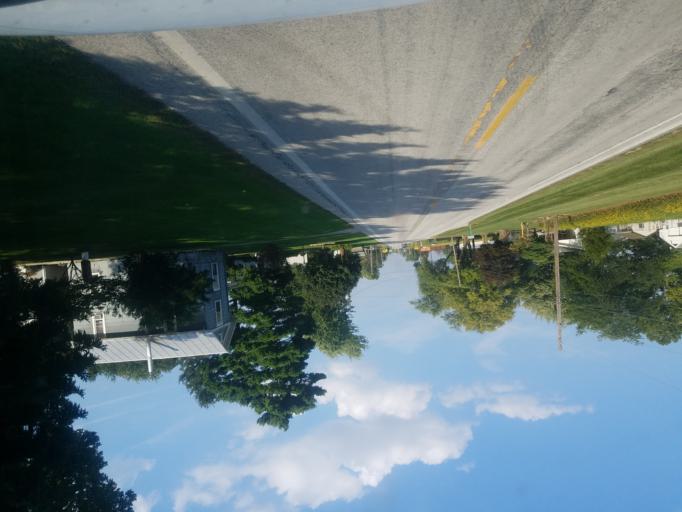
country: US
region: Ohio
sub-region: Hancock County
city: Arlington
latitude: 40.8911
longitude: -83.5626
